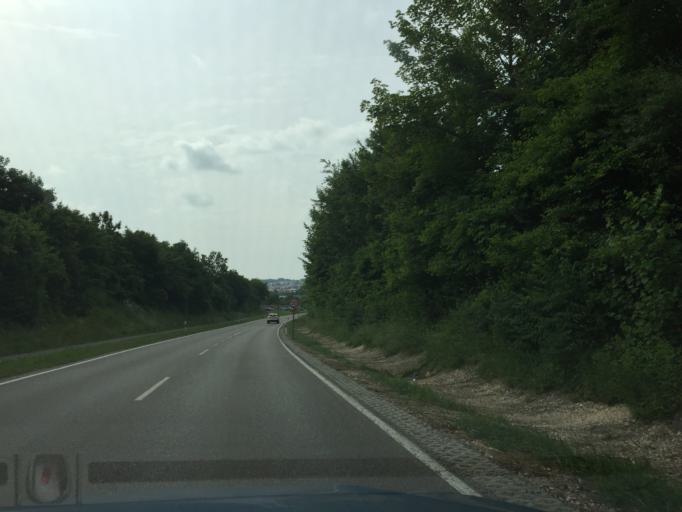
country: DE
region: Baden-Wuerttemberg
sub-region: Tuebingen Region
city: Ulm
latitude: 48.4093
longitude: 9.9457
